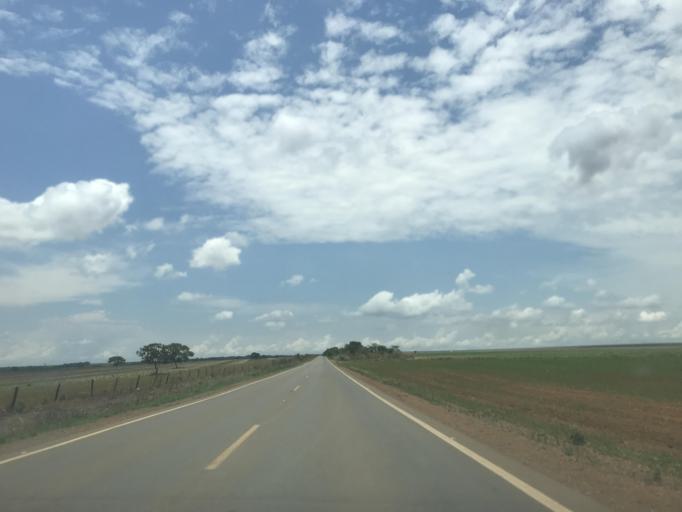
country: BR
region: Goias
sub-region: Luziania
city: Luziania
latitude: -16.5019
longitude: -48.2129
